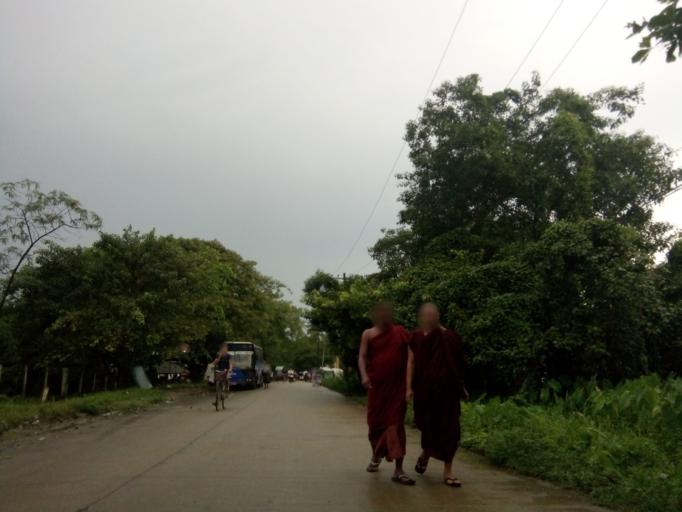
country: MM
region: Yangon
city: Yangon
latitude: 16.9176
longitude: 96.1594
